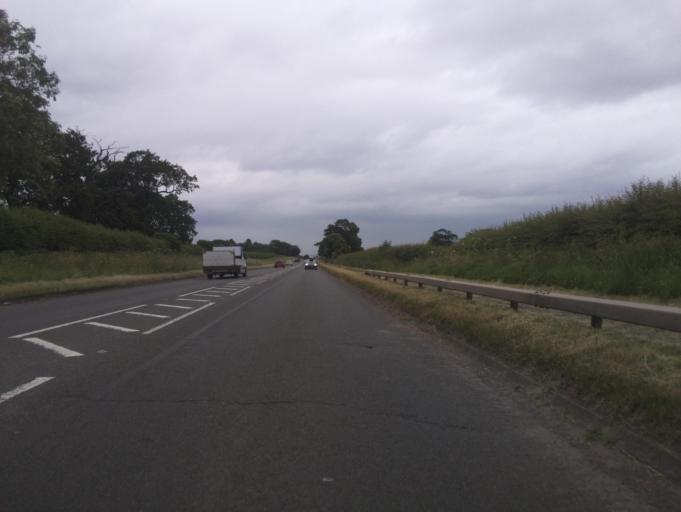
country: GB
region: England
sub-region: Staffordshire
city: Penkridge
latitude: 52.7498
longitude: -2.1071
